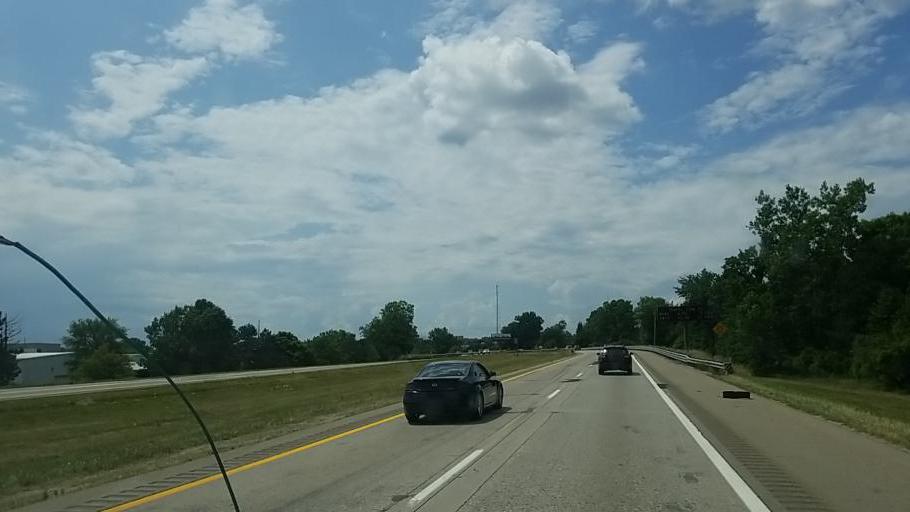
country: US
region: Michigan
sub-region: Kent County
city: East Grand Rapids
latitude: 42.9769
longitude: -85.6215
